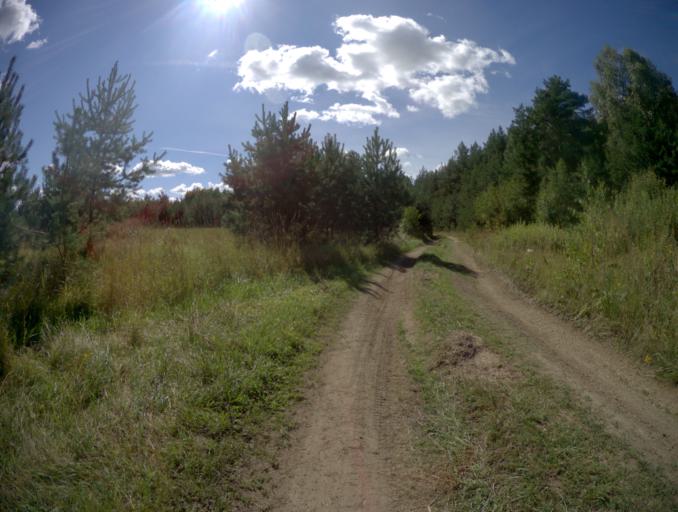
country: RU
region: Vladimir
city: Krasnaya Gorbatka
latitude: 55.8690
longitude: 41.8424
